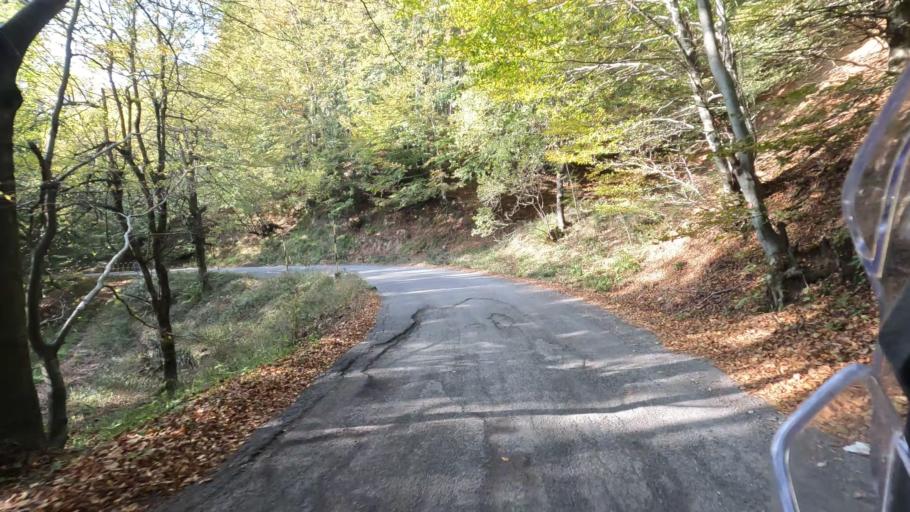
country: IT
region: Liguria
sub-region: Provincia di Savona
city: Urbe
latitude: 44.4303
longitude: 8.5536
